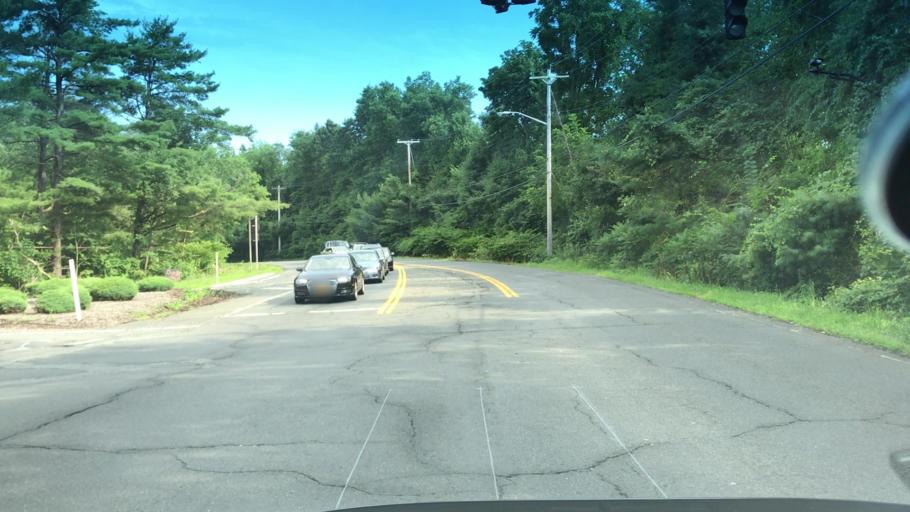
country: US
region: New York
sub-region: Rockland County
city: Bardonia
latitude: 41.1219
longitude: -74.0099
